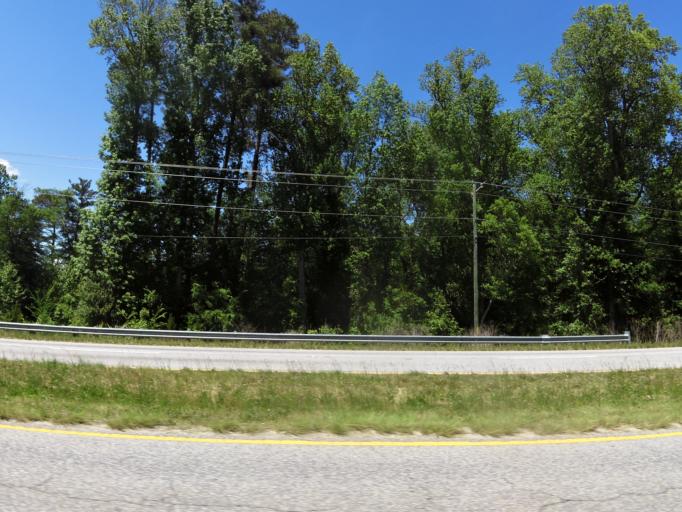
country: US
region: South Carolina
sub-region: Aiken County
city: Clearwater
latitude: 33.5055
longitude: -81.8927
